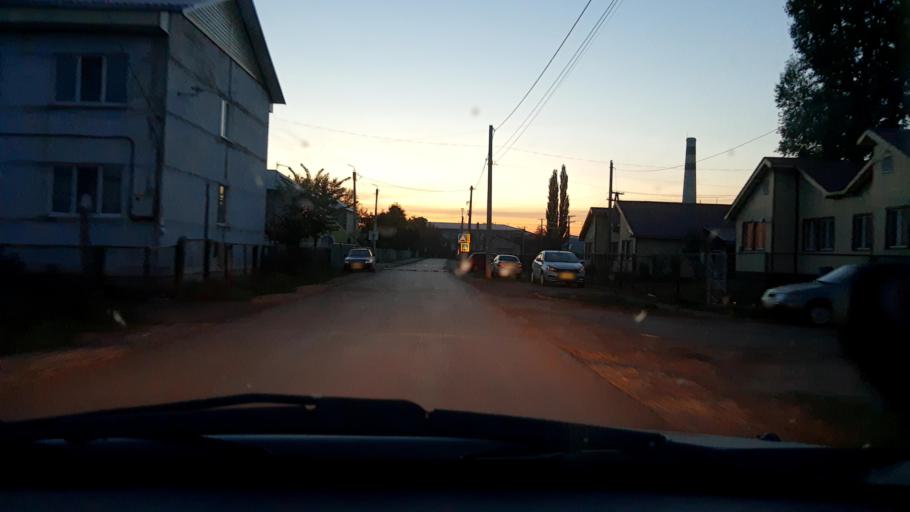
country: RU
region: Bashkortostan
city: Ulukulevo
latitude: 54.4244
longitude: 56.3331
